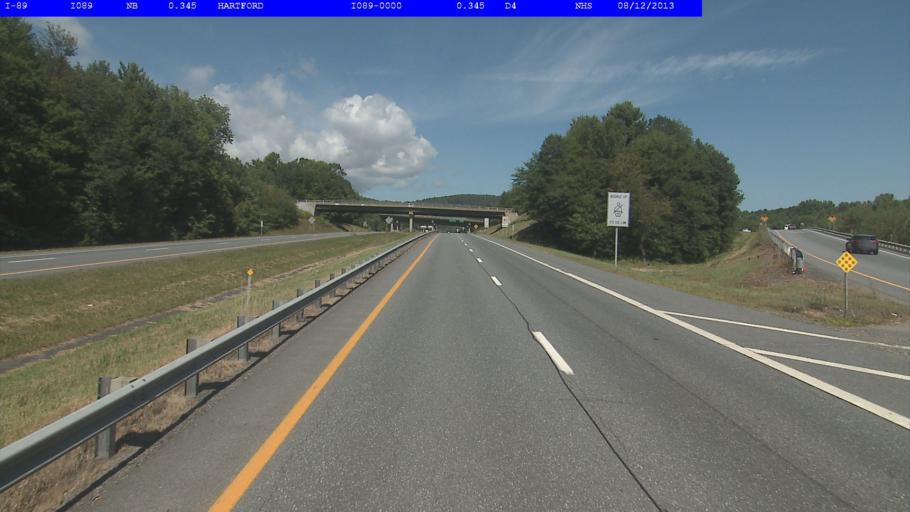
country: US
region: Vermont
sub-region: Windsor County
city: White River Junction
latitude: 43.6378
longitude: -72.3349
